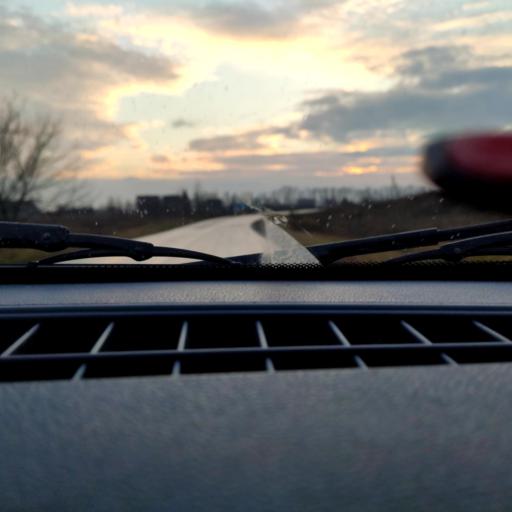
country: RU
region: Bashkortostan
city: Avdon
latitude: 54.5098
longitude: 55.8405
